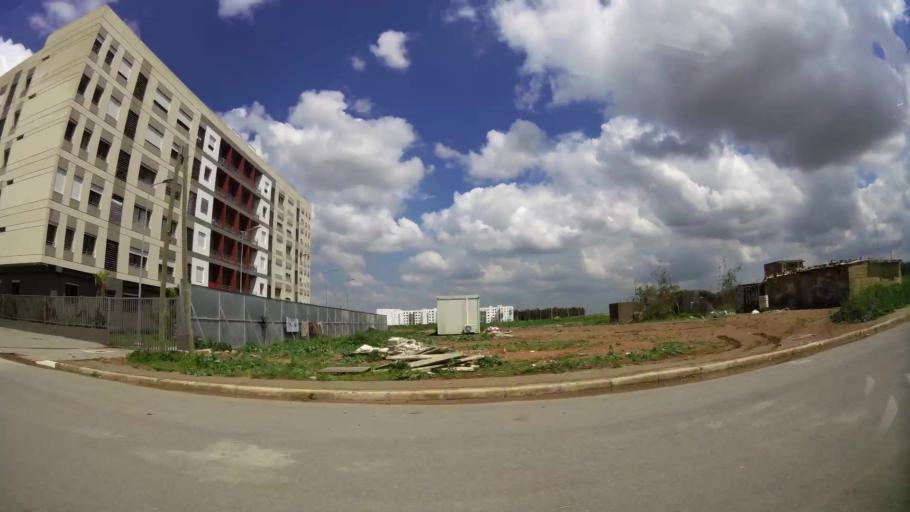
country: MA
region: Chaouia-Ouardigha
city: Nouaseur
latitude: 33.3879
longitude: -7.5601
